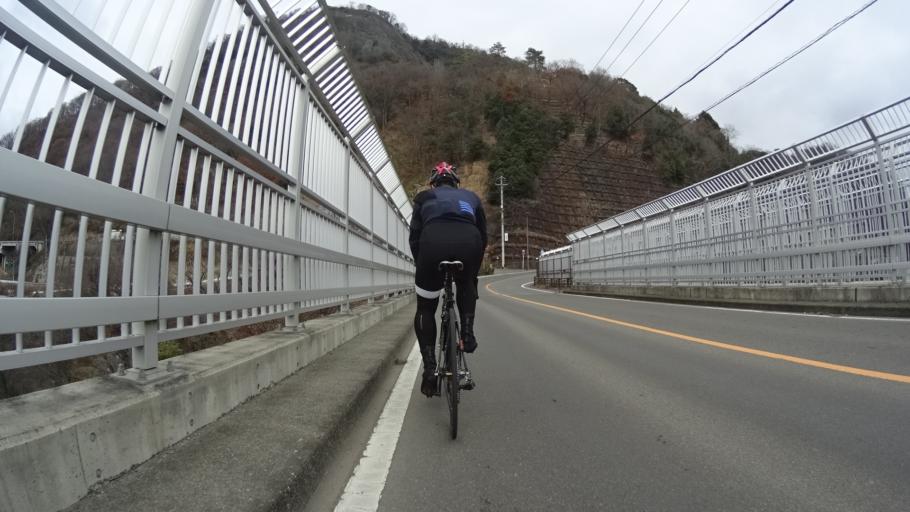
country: JP
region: Yamanashi
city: Otsuki
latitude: 35.6175
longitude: 138.9486
